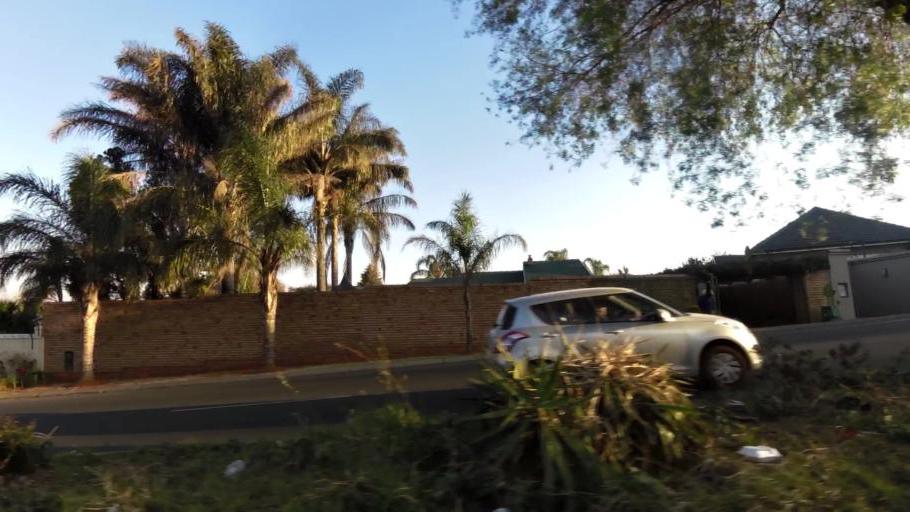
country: ZA
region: Gauteng
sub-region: City of Johannesburg Metropolitan Municipality
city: Roodepoort
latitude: -26.1672
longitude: 27.9604
